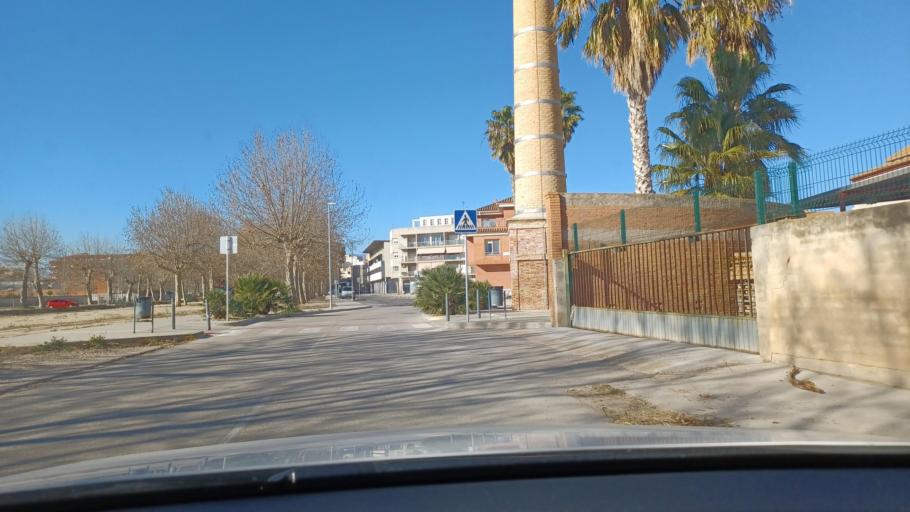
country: ES
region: Catalonia
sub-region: Provincia de Tarragona
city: Amposta
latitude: 40.7098
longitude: 0.5860
